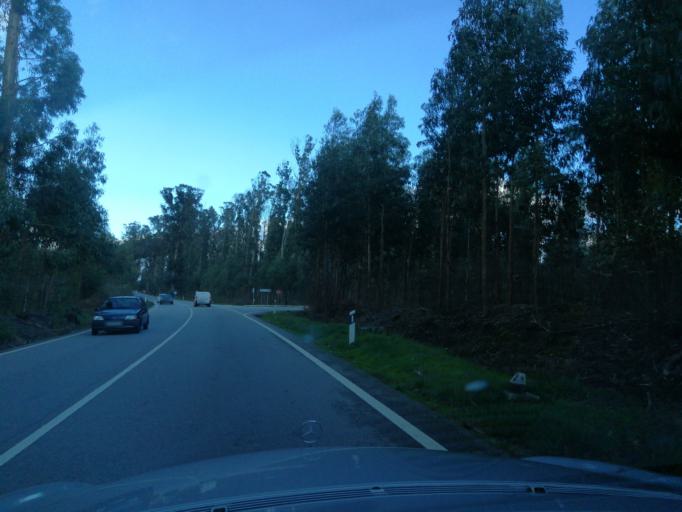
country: PT
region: Braga
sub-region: Esposende
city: Marinhas
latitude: 41.5729
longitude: -8.7174
